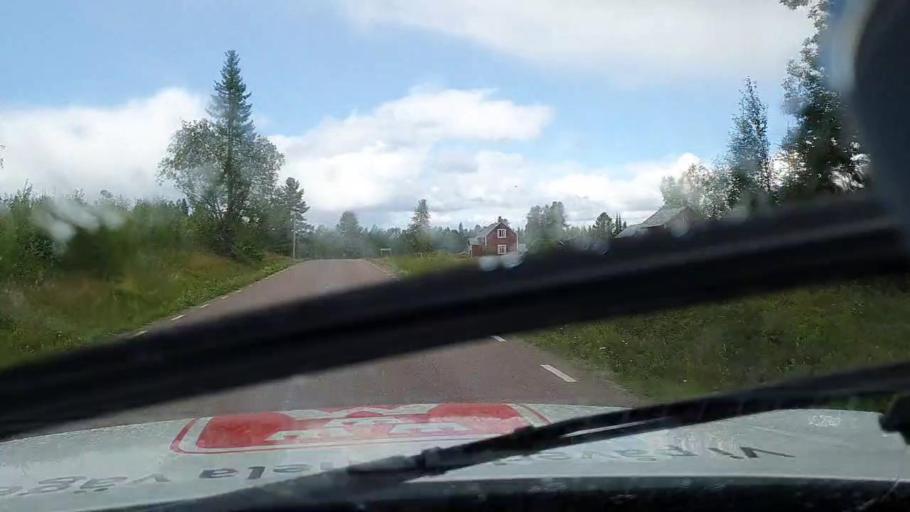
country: SE
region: Jaemtland
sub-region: Stroemsunds Kommun
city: Stroemsund
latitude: 63.8764
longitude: 15.3590
